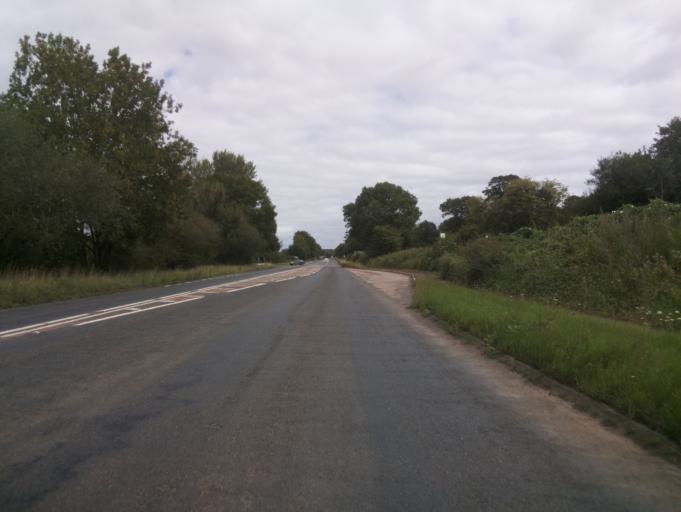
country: GB
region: England
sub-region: Devon
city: Bradninch
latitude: 50.8090
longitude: -3.4241
